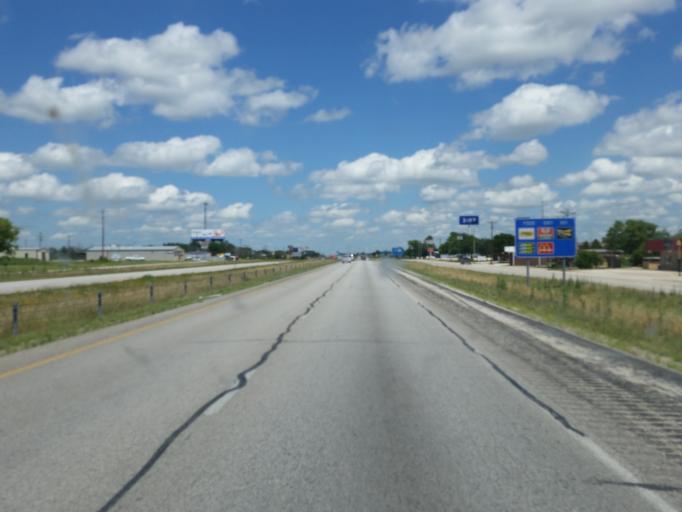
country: US
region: Texas
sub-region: Callahan County
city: Clyde
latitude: 32.4138
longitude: -99.5007
